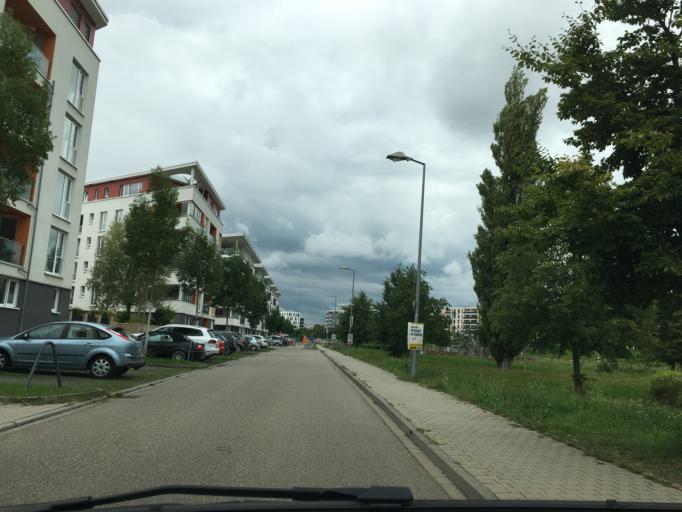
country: DE
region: Baden-Wuerttemberg
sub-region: Karlsruhe Region
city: Karlsruhe
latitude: 49.0012
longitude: 8.4213
